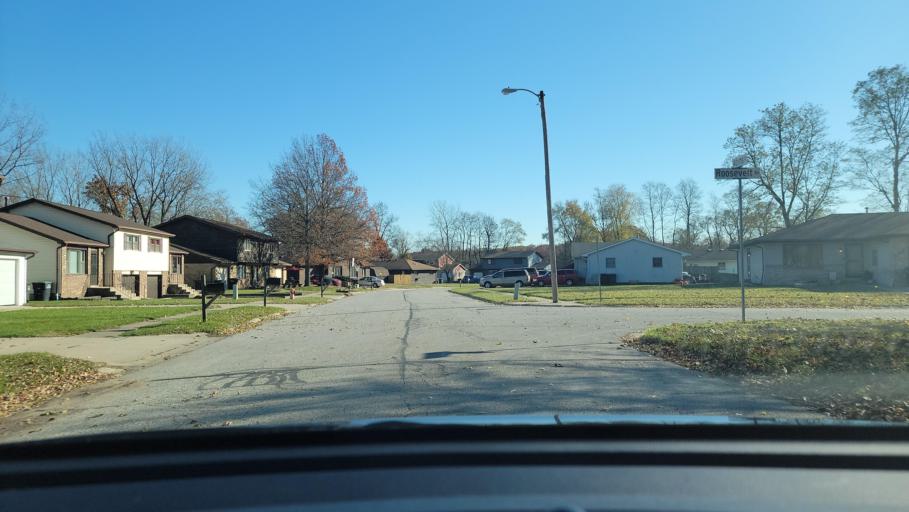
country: US
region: Indiana
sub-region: Porter County
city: Burns Harbor
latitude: 41.5983
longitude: -87.1465
